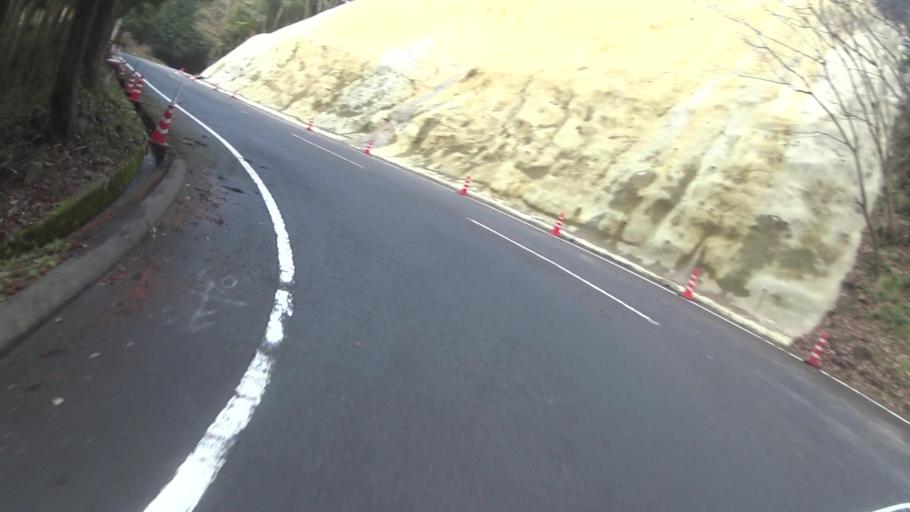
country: JP
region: Kyoto
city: Maizuru
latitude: 35.4366
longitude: 135.3946
